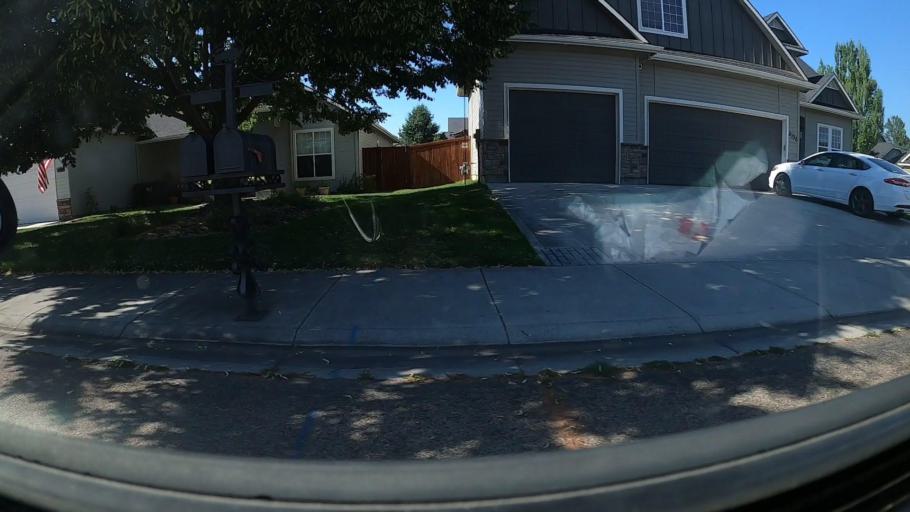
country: US
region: Idaho
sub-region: Ada County
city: Meridian
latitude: 43.6286
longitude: -116.3655
